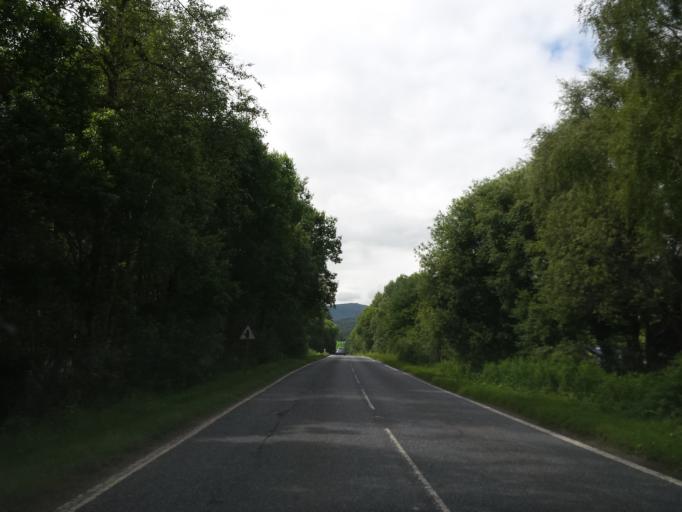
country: GB
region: Scotland
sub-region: Highland
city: Fort William
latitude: 56.8471
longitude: -5.1578
